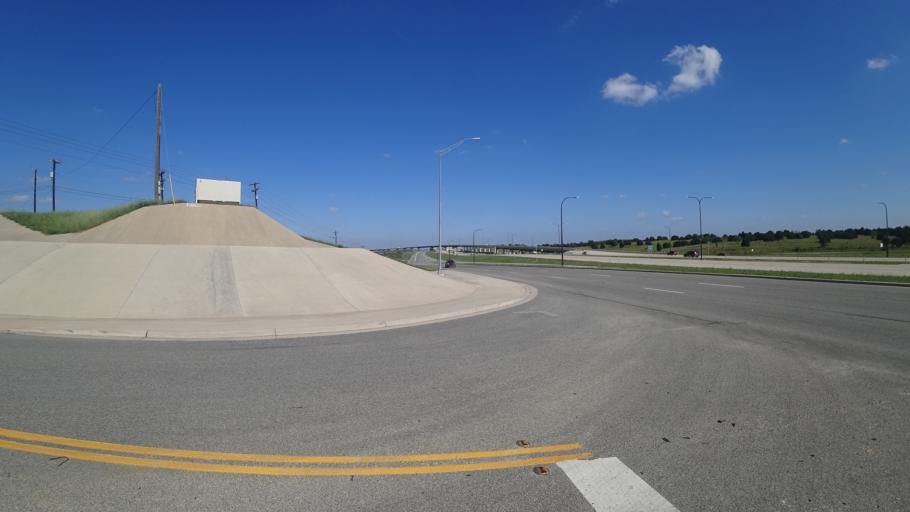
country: US
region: Texas
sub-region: Travis County
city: Manor
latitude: 30.3368
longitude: -97.6026
